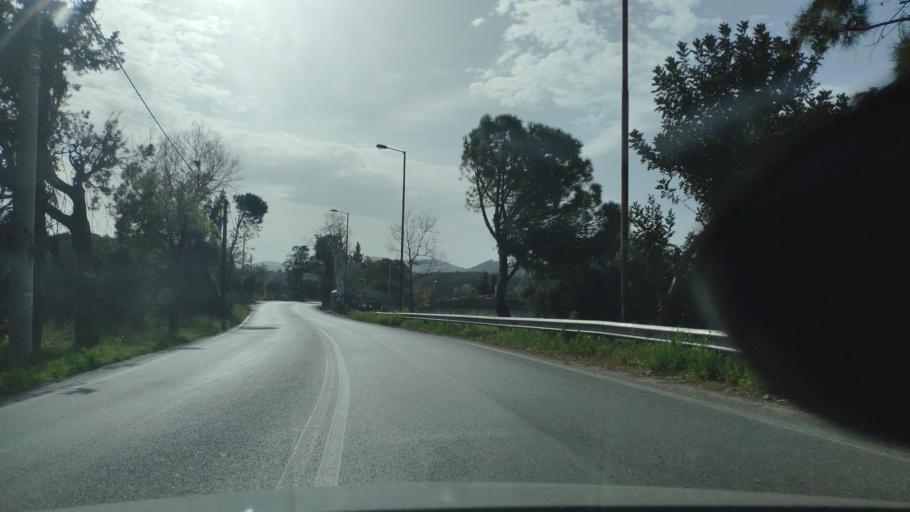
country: GR
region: Attica
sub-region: Nomarchia Anatolikis Attikis
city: Limin Mesoyaias
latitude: 37.8944
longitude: 23.9832
